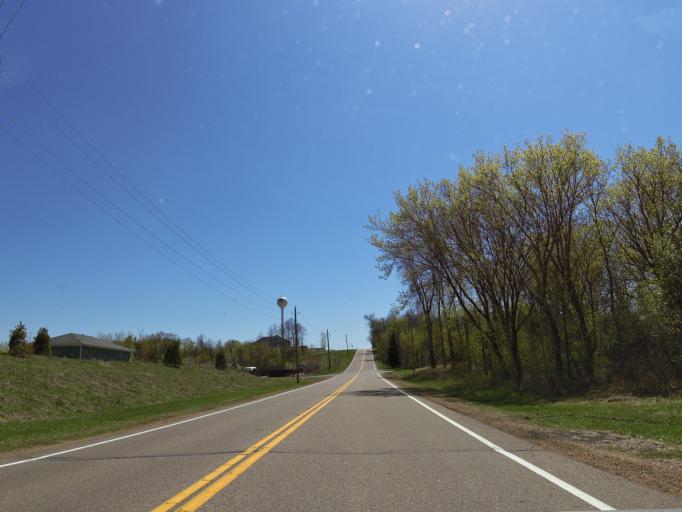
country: US
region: Minnesota
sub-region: Scott County
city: Prior Lake
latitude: 44.7578
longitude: -93.4494
